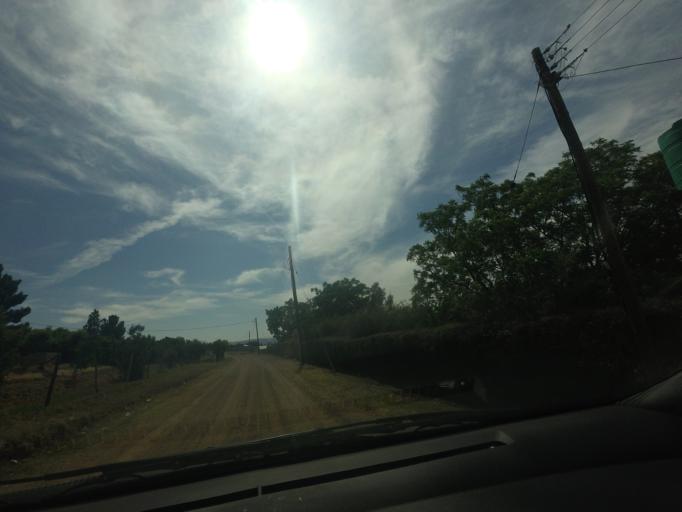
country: LS
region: Berea
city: Teyateyaneng
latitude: -29.1531
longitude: 27.7521
